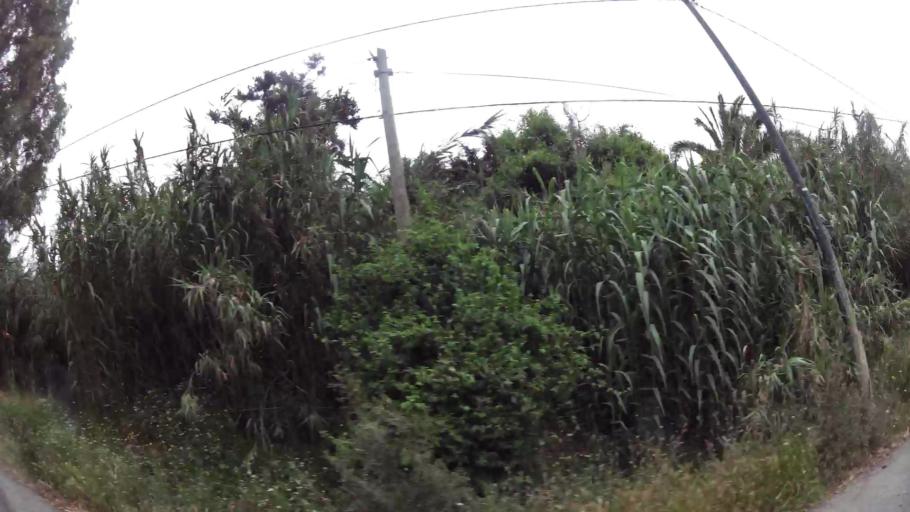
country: MA
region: Rabat-Sale-Zemmour-Zaer
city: Sale
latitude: 33.9956
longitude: -6.7706
